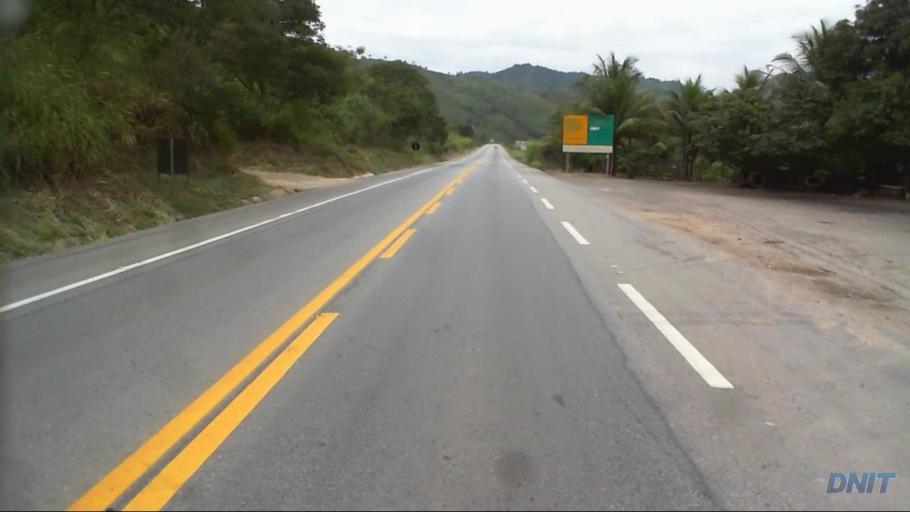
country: BR
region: Minas Gerais
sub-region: Timoteo
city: Timoteo
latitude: -19.6135
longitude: -42.7700
